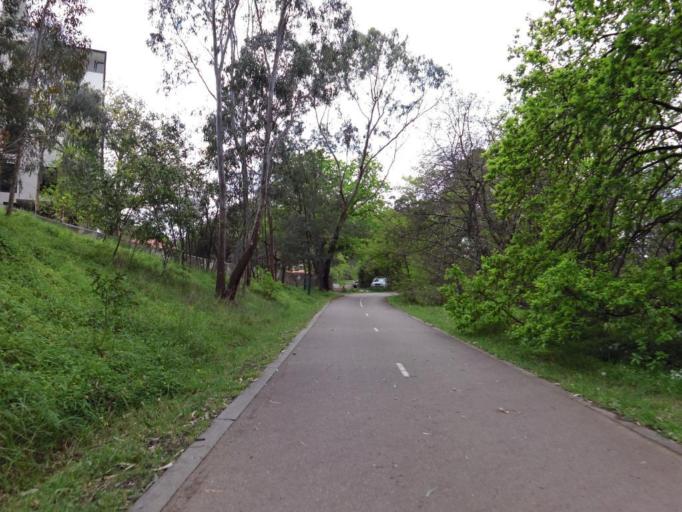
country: AU
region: Victoria
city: Rosanna
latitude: -37.7579
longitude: 145.0730
